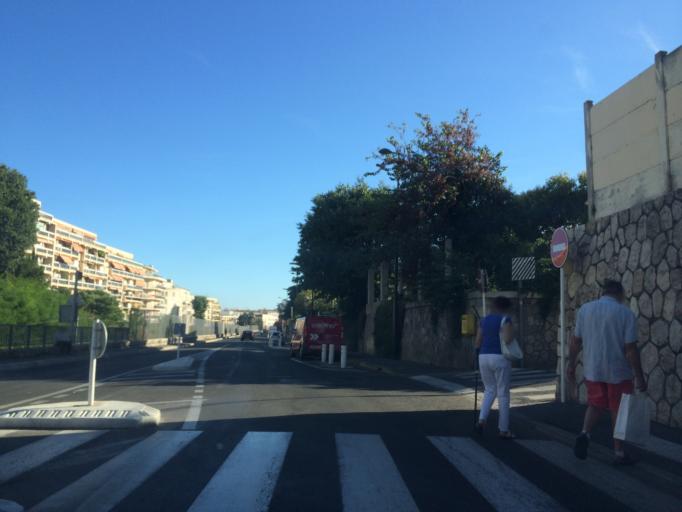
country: FR
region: Provence-Alpes-Cote d'Azur
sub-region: Departement des Alpes-Maritimes
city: Antibes
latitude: 43.5752
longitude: 7.1159
